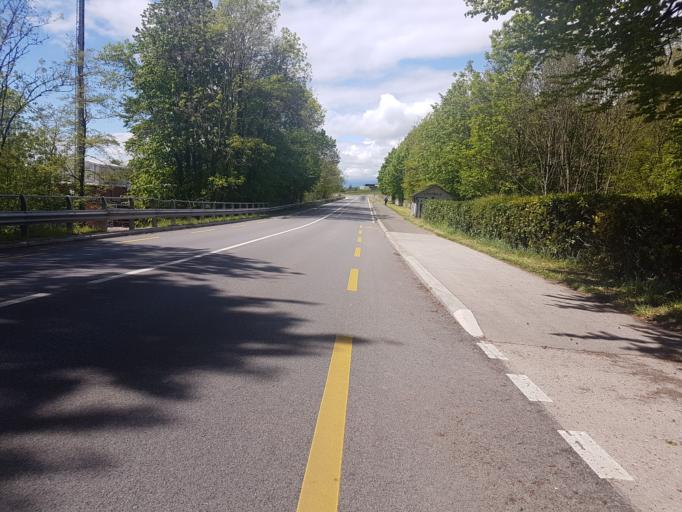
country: CH
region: Vaud
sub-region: Nyon District
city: Gland
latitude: 46.4268
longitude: 6.2957
